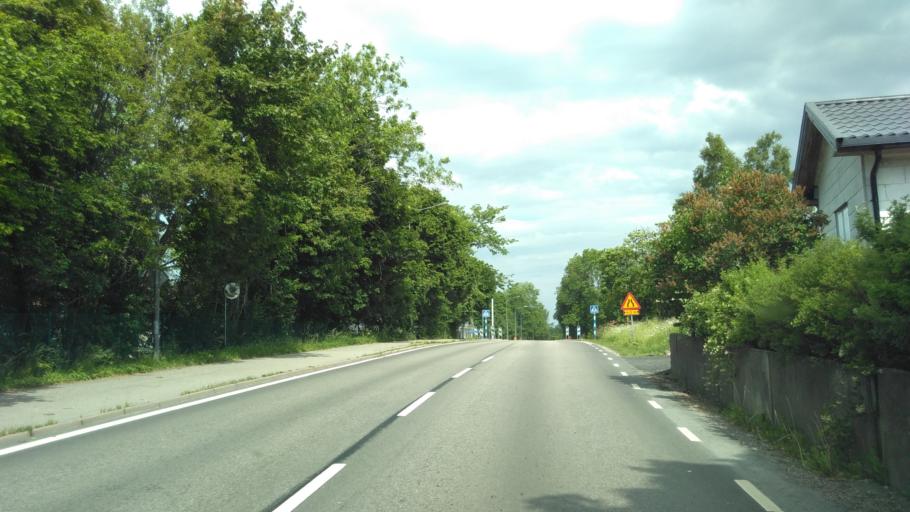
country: SE
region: Vaestra Goetaland
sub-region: Vara Kommun
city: Kvanum
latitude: 58.3797
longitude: 13.1475
